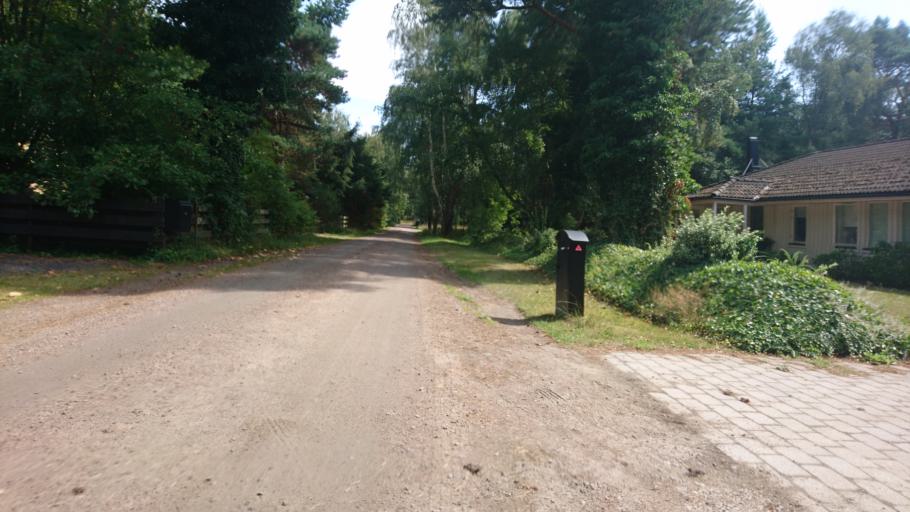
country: SE
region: Skane
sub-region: Vellinge Kommun
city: Ljunghusen
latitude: 55.4042
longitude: 12.9110
